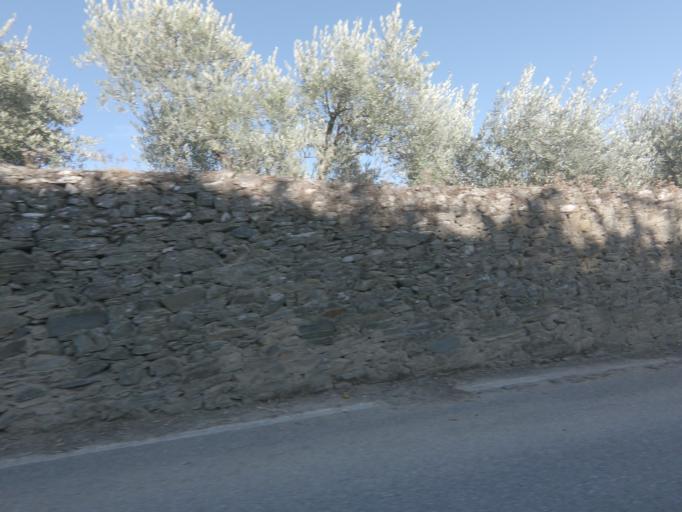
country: PT
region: Vila Real
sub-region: Peso da Regua
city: Peso da Regua
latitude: 41.1784
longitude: -7.7805
